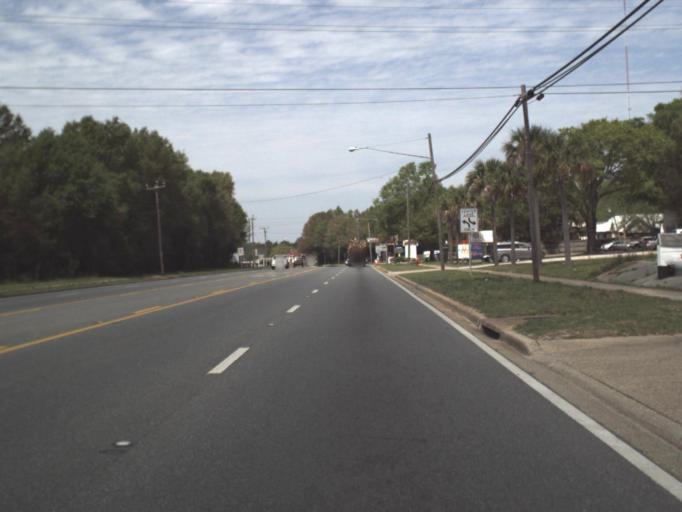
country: US
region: Florida
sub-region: Okaloosa County
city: Crestview
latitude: 30.7641
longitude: -86.5811
